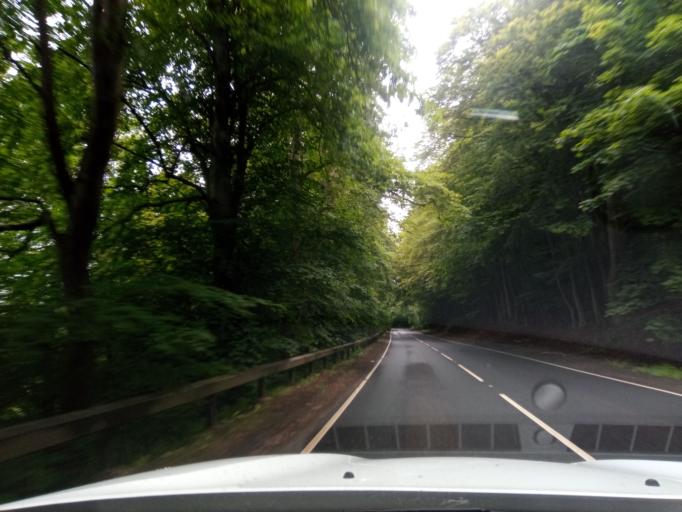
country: GB
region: Scotland
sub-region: The Scottish Borders
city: Earlston
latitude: 55.6499
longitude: -2.6915
